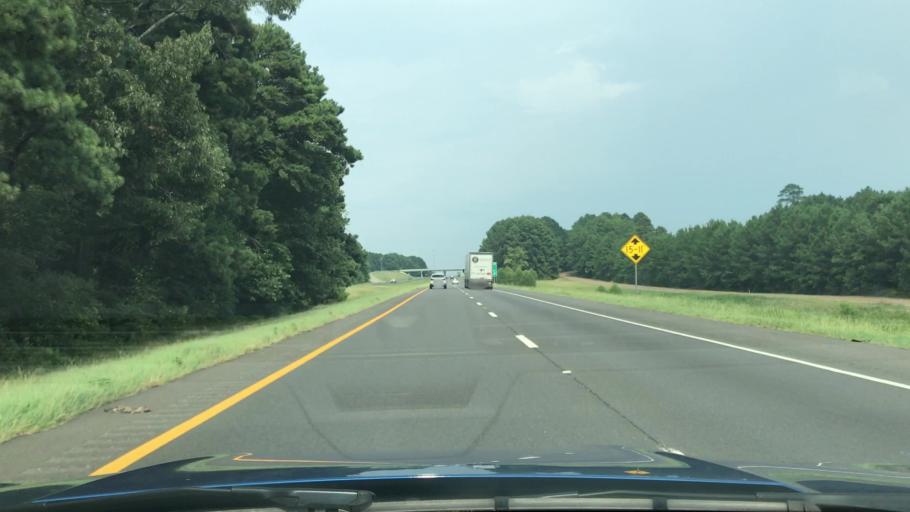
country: US
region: Texas
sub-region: Harrison County
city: Hallsville
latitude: 32.4717
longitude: -94.5874
